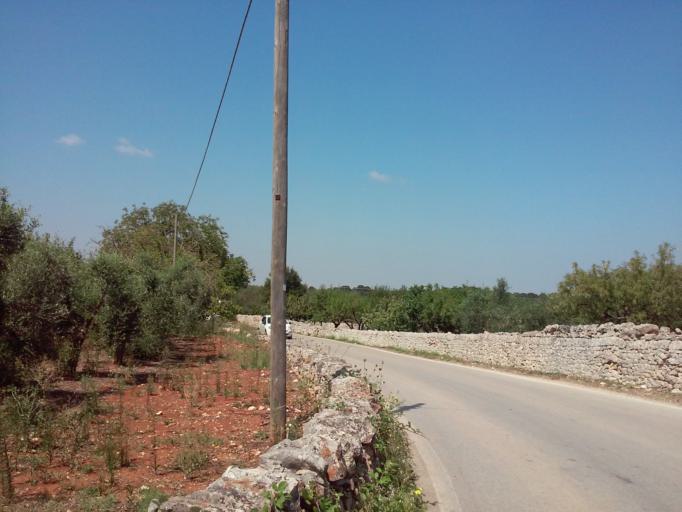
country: IT
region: Apulia
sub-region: Provincia di Bari
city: Alberobello
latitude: 40.7959
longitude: 17.2202
